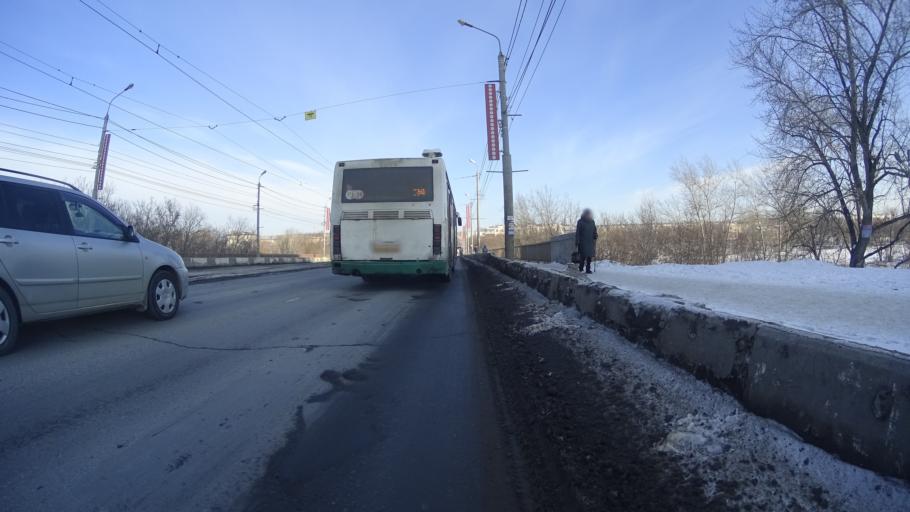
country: RU
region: Chelyabinsk
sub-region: Gorod Chelyabinsk
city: Chelyabinsk
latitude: 55.1849
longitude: 61.4094
